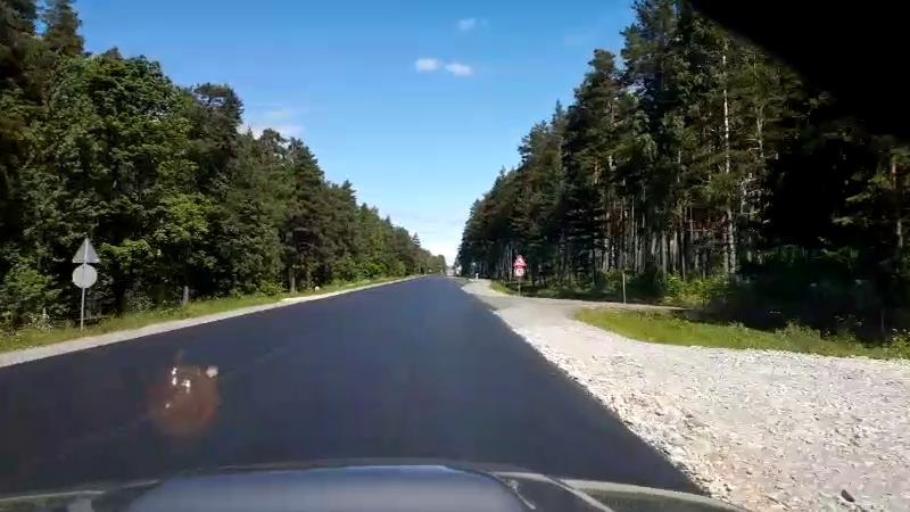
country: LV
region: Salacgrivas
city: Ainazi
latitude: 57.8458
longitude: 24.3510
